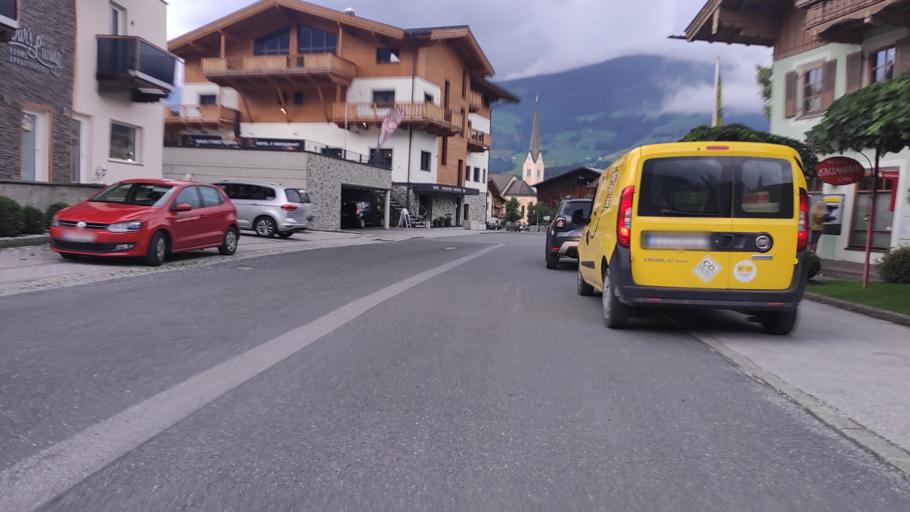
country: AT
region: Salzburg
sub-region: Politischer Bezirk Zell am See
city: Hollersbach im Pinzgau
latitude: 47.2740
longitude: 12.4214
